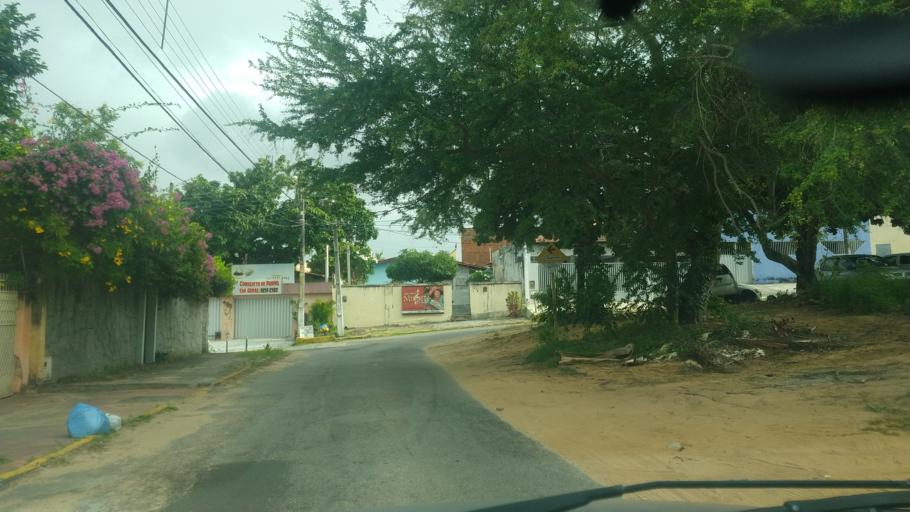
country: BR
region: Rio Grande do Norte
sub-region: Natal
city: Natal
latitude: -5.8276
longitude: -35.2075
